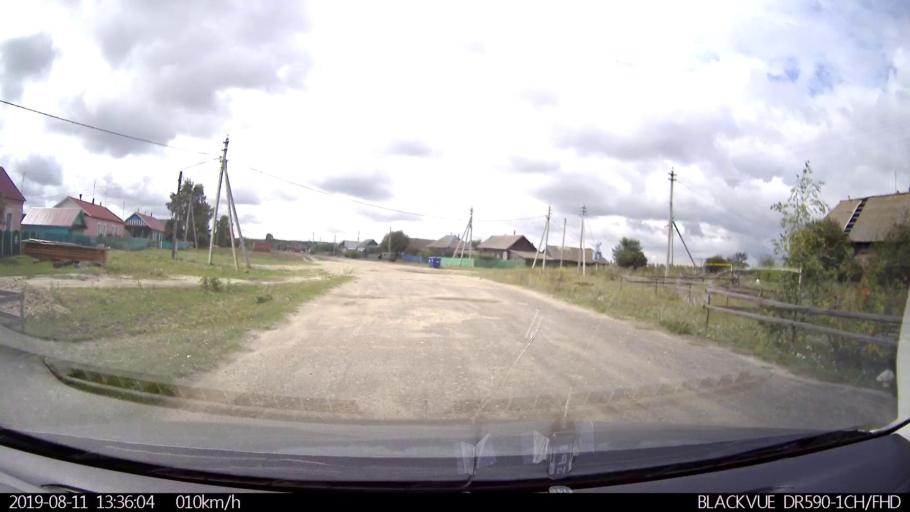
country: RU
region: Ulyanovsk
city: Ignatovka
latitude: 53.8599
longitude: 47.5872
